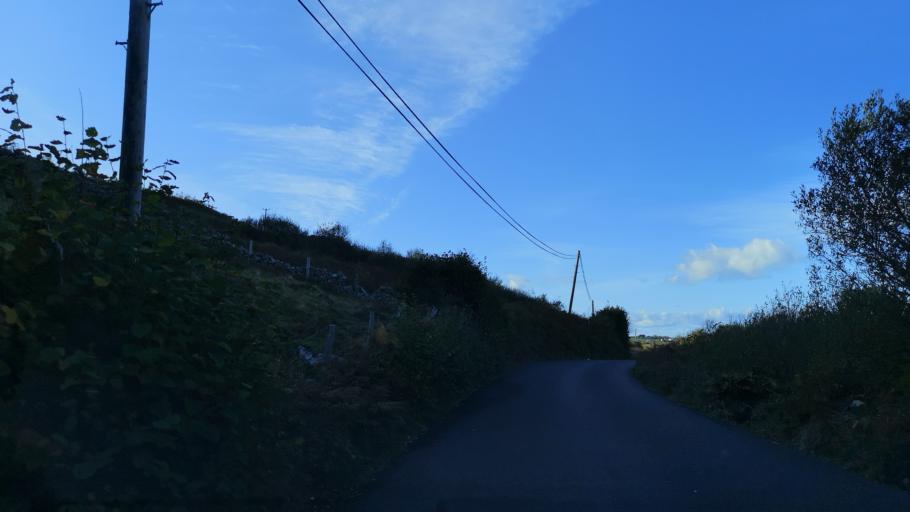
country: IE
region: Connaught
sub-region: County Galway
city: Clifden
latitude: 53.5044
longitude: -10.0707
